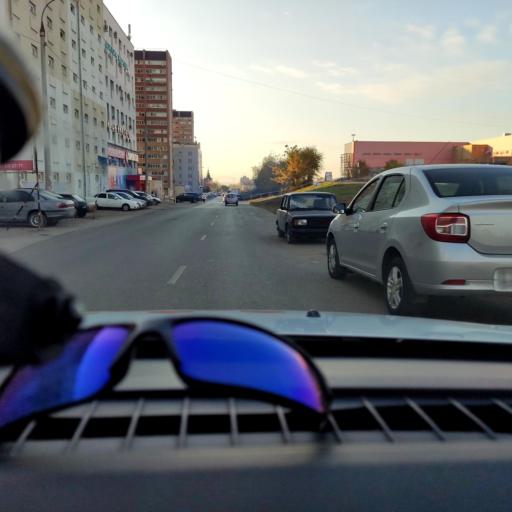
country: RU
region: Samara
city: Samara
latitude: 53.2095
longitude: 50.2029
